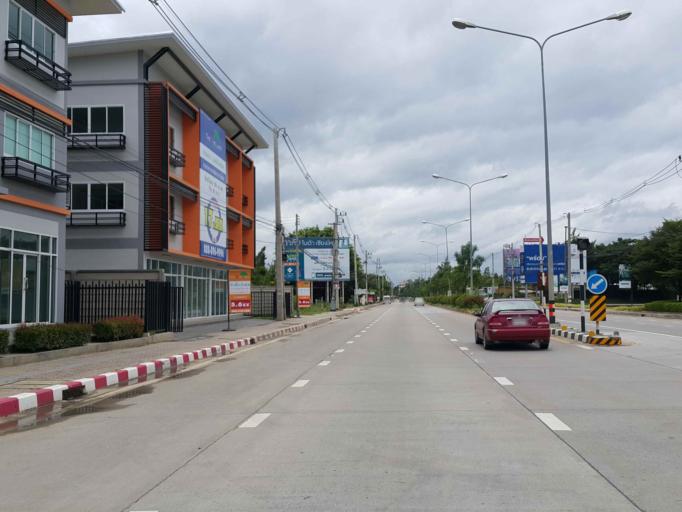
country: TH
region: Chiang Mai
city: San Sai
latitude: 18.8407
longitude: 98.9983
